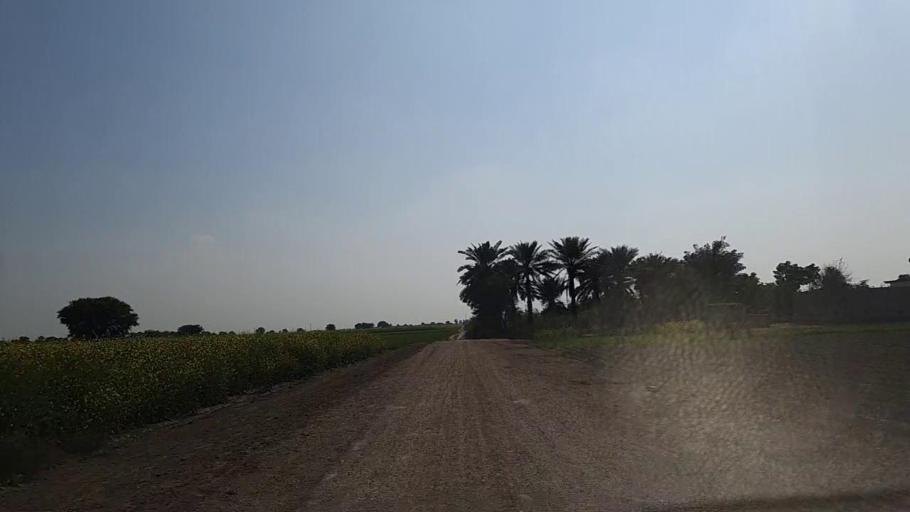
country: PK
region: Sindh
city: Jam Sahib
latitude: 26.2432
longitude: 68.5667
